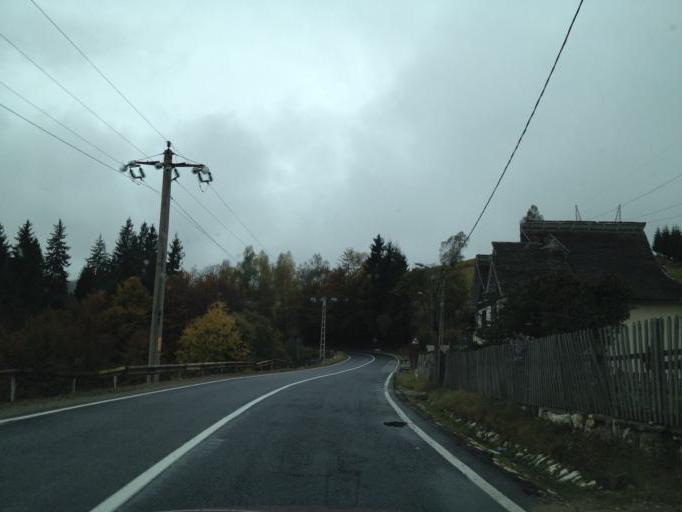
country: RO
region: Brasov
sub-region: Comuna Fundata
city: Fundata
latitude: 45.4608
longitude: 25.2867
